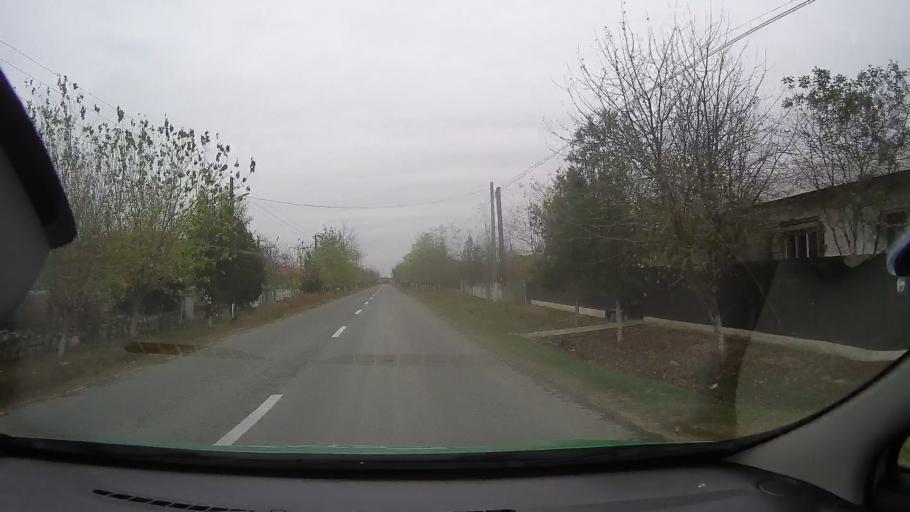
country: RO
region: Constanta
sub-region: Comuna Crucea
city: Crucea
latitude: 44.4481
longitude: 28.2405
